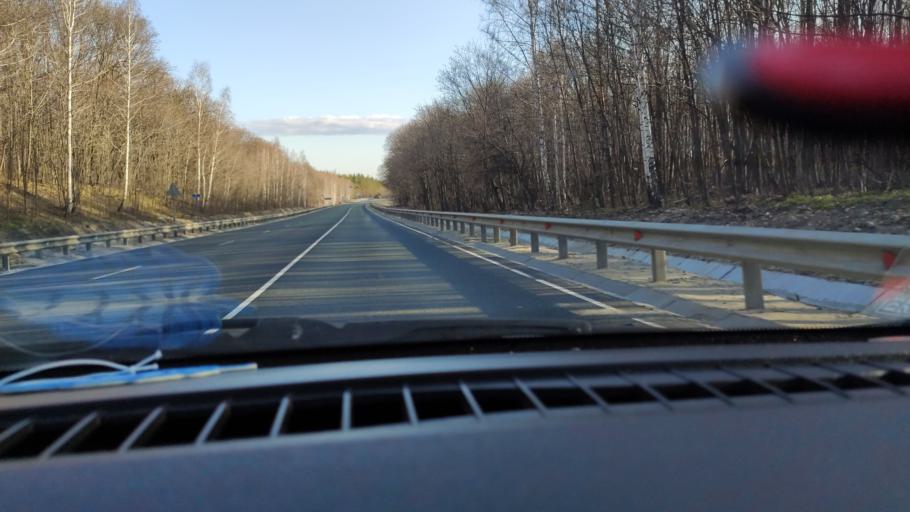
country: RU
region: Saratov
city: Khvalynsk
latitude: 52.5109
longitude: 48.0161
